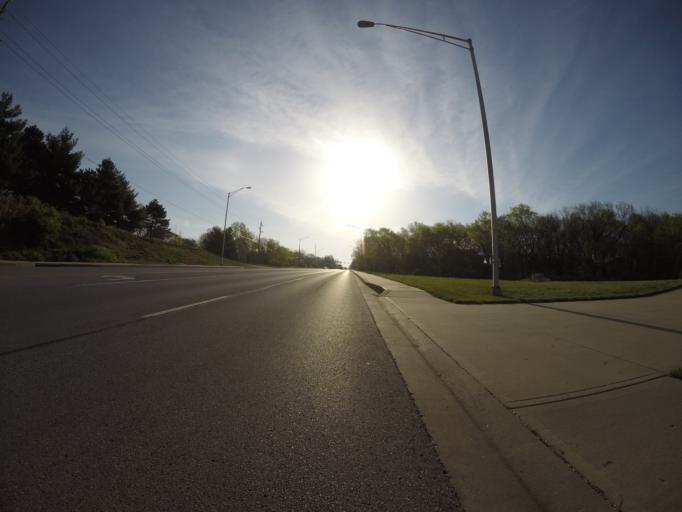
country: US
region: Missouri
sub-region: Jackson County
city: Lees Summit
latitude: 38.9119
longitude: -94.4164
